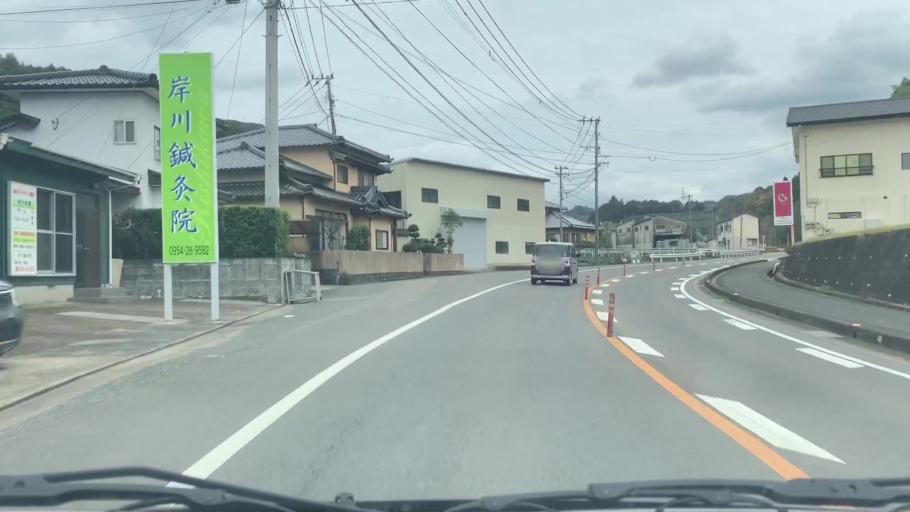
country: JP
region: Saga Prefecture
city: Ureshinomachi-shimojuku
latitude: 33.1004
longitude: 130.0004
